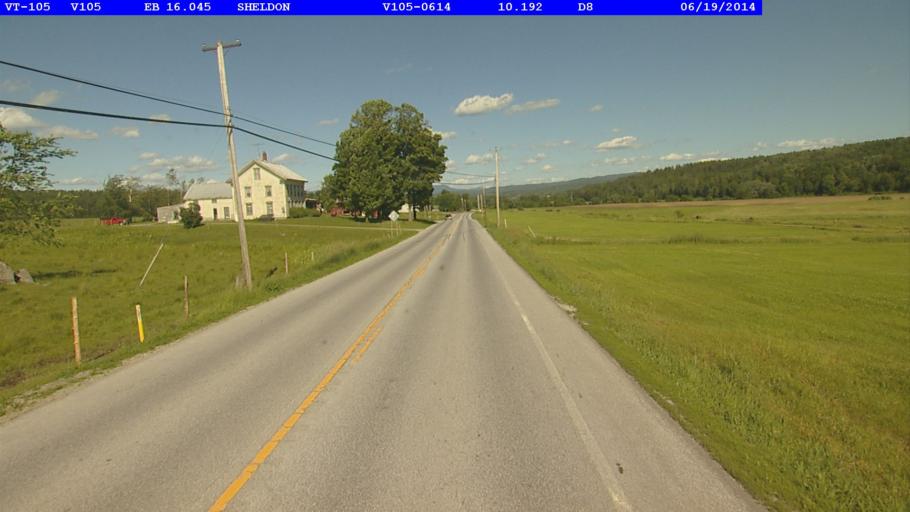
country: US
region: Vermont
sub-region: Franklin County
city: Enosburg Falls
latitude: 44.9074
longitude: -72.8363
